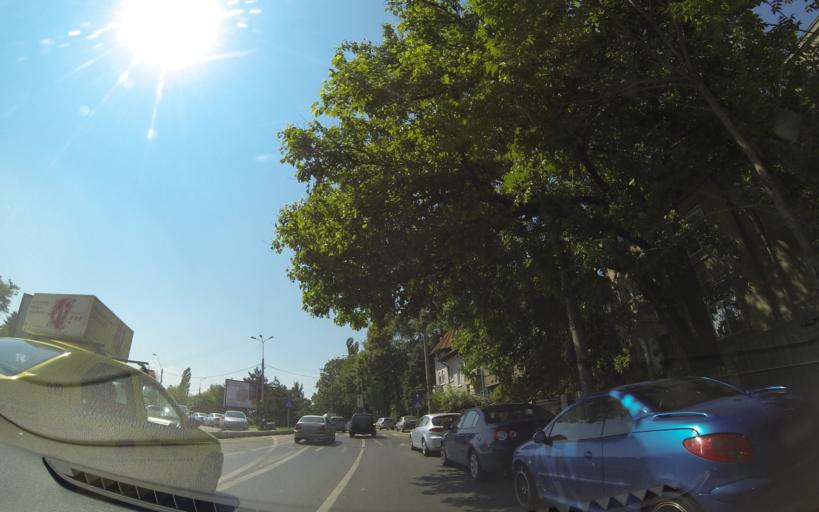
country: RO
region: Bucuresti
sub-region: Municipiul Bucuresti
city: Bucuresti
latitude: 44.4322
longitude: 26.0591
